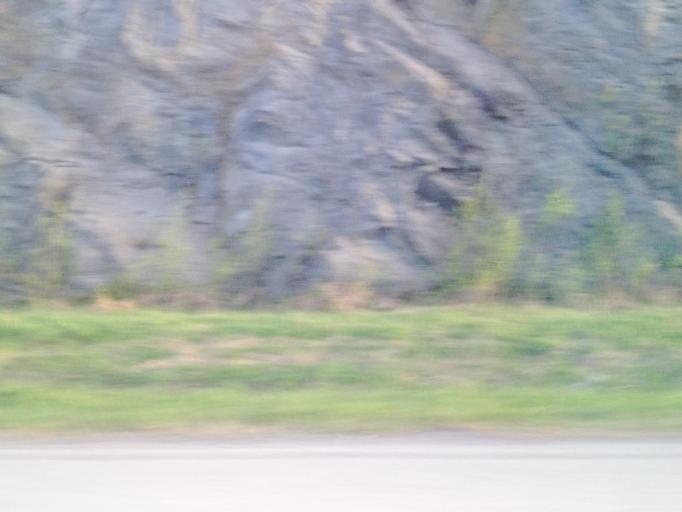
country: FI
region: Pirkanmaa
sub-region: Etelae-Pirkanmaa
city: Akaa
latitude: 61.1759
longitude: 23.9149
